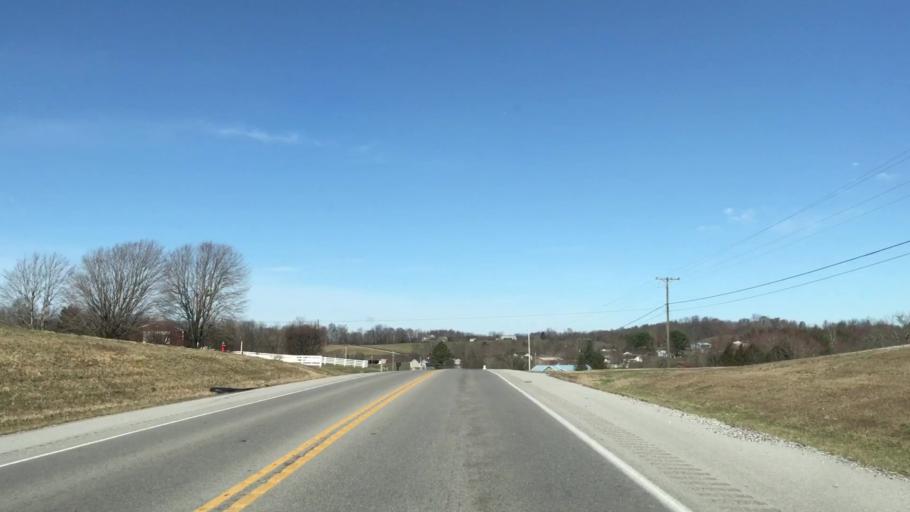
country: US
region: Kentucky
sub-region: Barren County
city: Glasgow
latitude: 36.9297
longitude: -85.8112
